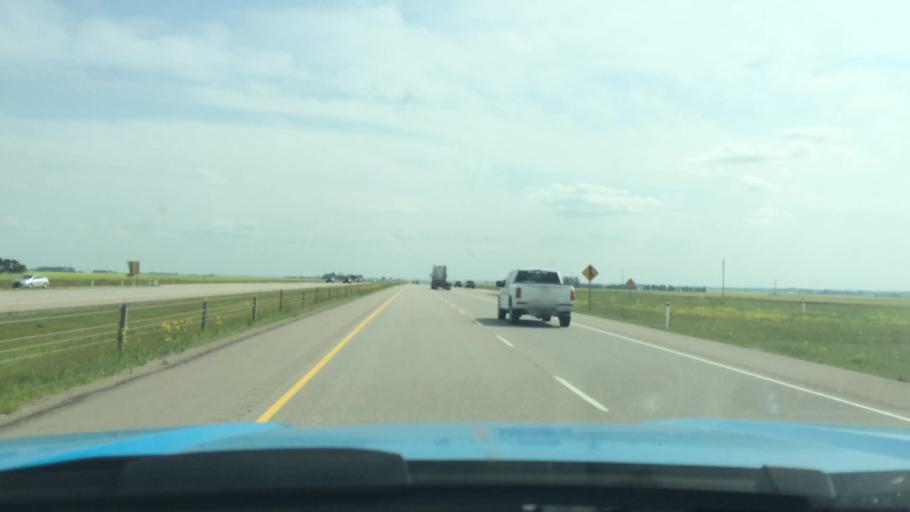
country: CA
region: Alberta
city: Didsbury
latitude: 51.6619
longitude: -114.0257
